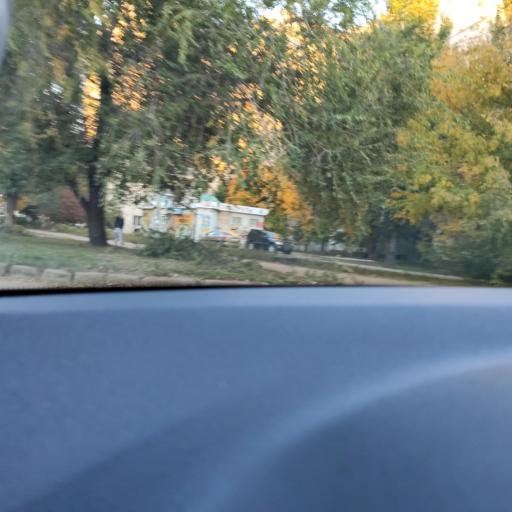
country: RU
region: Samara
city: Samara
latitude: 53.2110
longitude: 50.2549
